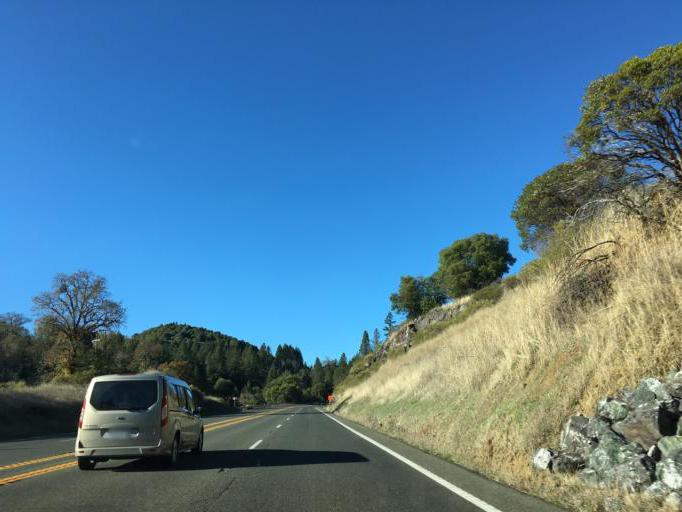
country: US
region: California
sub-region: Mendocino County
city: Laytonville
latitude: 39.6171
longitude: -123.4620
